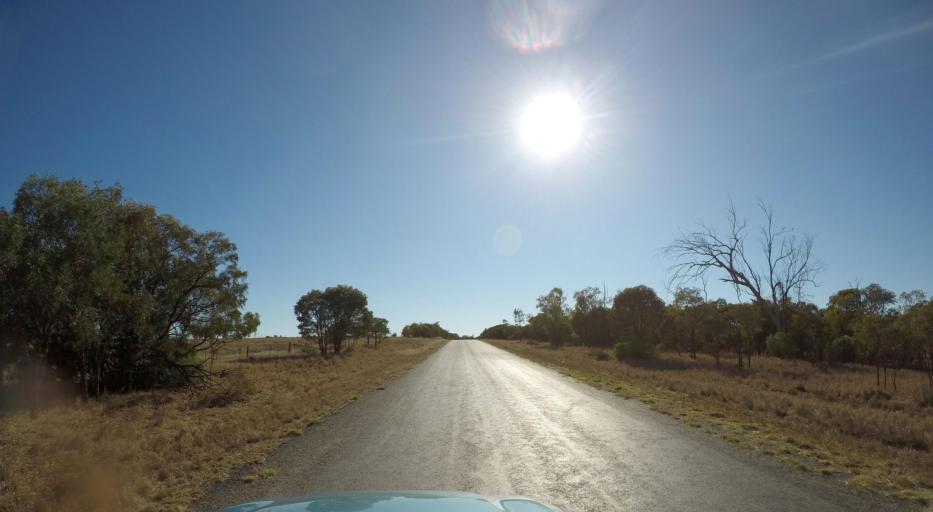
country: AU
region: Queensland
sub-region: Banana
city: Taroom
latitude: -25.9978
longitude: 149.3578
